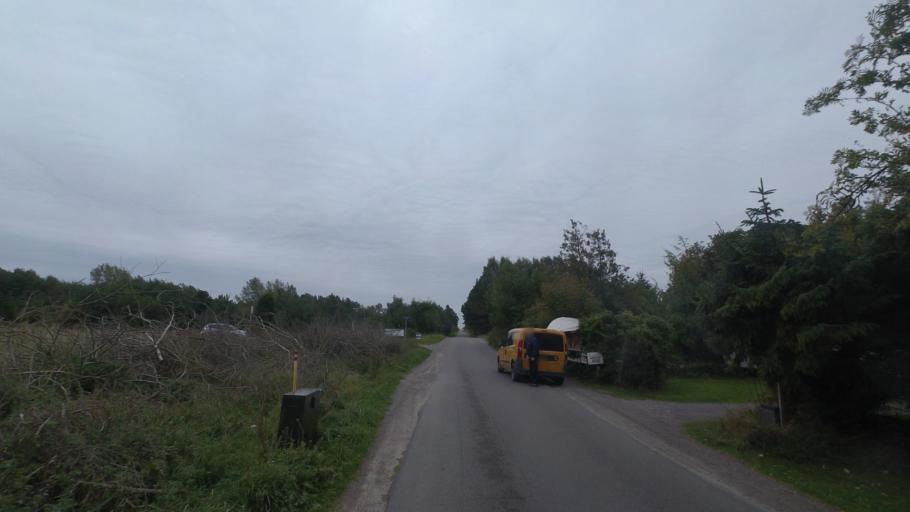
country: DK
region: Capital Region
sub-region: Bornholm Kommune
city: Akirkeby
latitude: 55.0043
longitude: 14.9925
